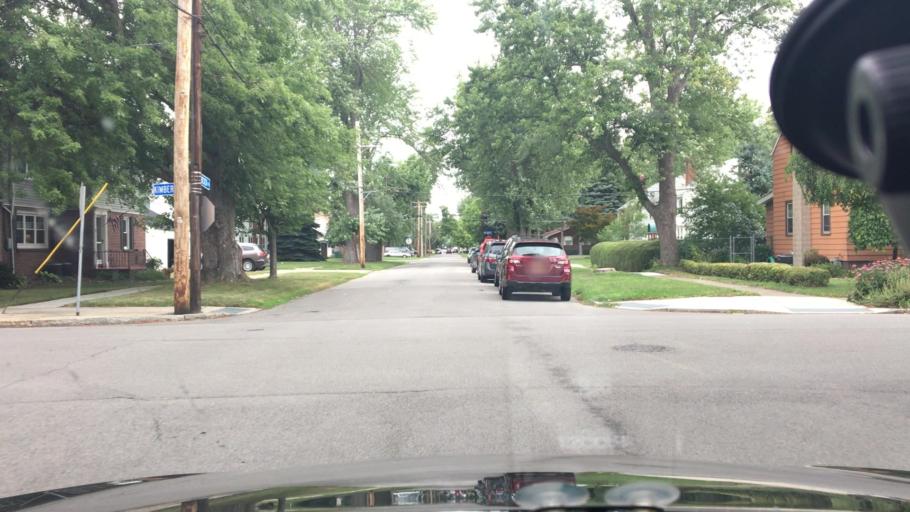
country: US
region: New York
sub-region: Erie County
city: Lackawanna
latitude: 42.8380
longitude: -78.8124
